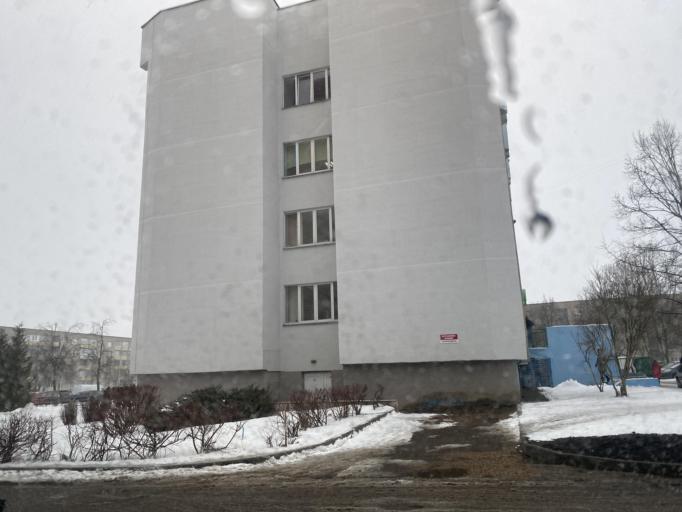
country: BY
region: Minsk
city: Horad Zhodzina
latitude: 54.0936
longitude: 28.3061
